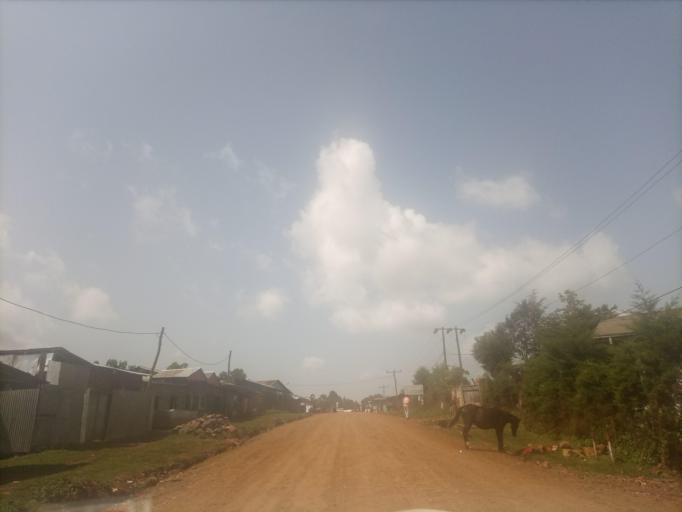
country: ET
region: Oromiya
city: Agaro
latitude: 7.7869
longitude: 36.4205
